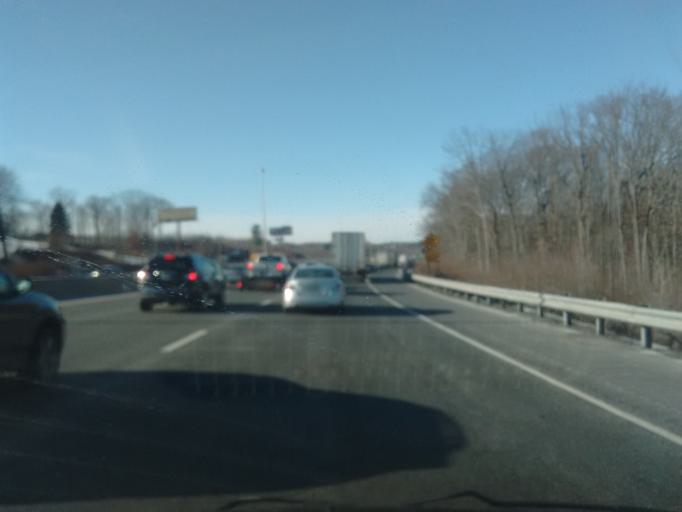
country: US
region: Connecticut
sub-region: New Haven County
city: Prospect
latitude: 41.5369
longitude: -72.9664
